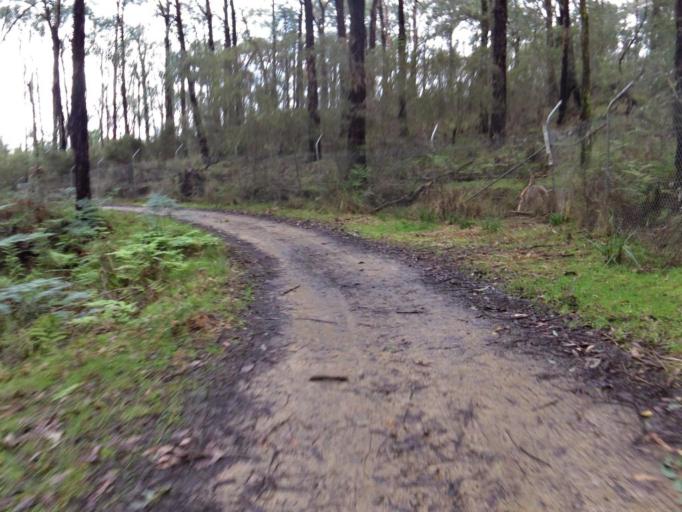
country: AU
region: Victoria
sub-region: Yarra Ranges
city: Lysterfield
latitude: -37.9321
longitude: 145.2816
